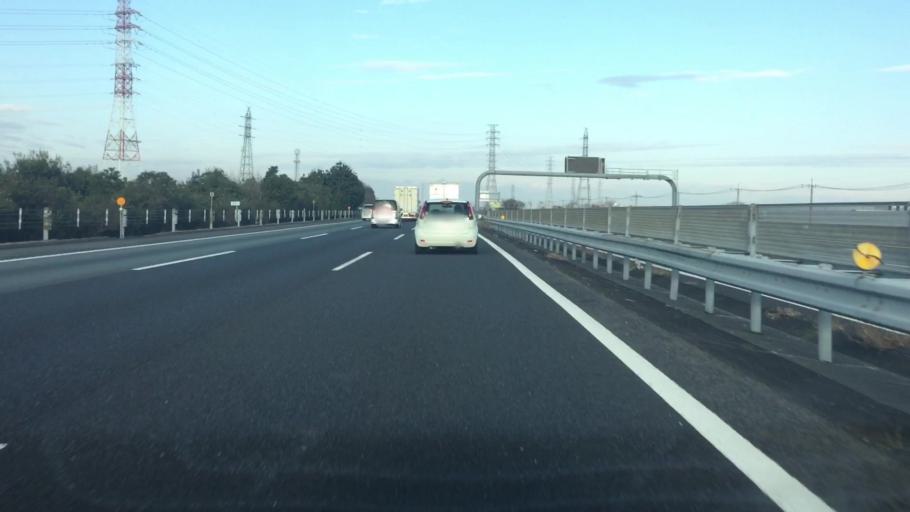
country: JP
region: Saitama
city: Honjo
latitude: 36.2226
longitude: 139.1610
